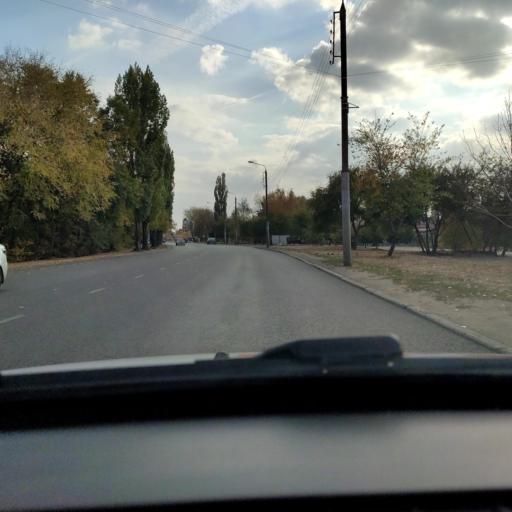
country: RU
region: Voronezj
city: Voronezh
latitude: 51.6218
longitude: 39.1761
